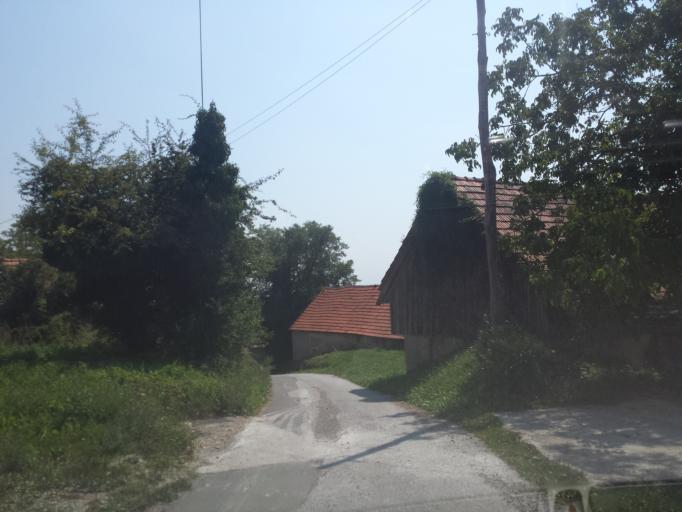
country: HR
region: Zagrebacka
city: Rude
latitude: 45.7259
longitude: 15.6701
